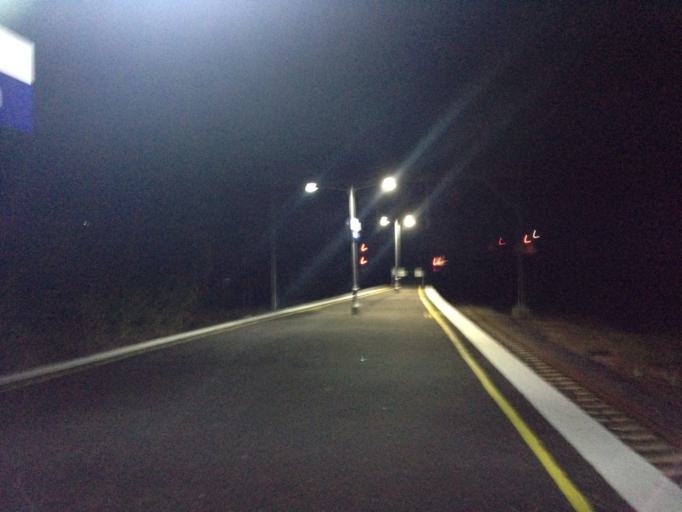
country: AU
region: New South Wales
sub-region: Ku-ring-gai
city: Killara
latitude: -33.7651
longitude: 151.1614
